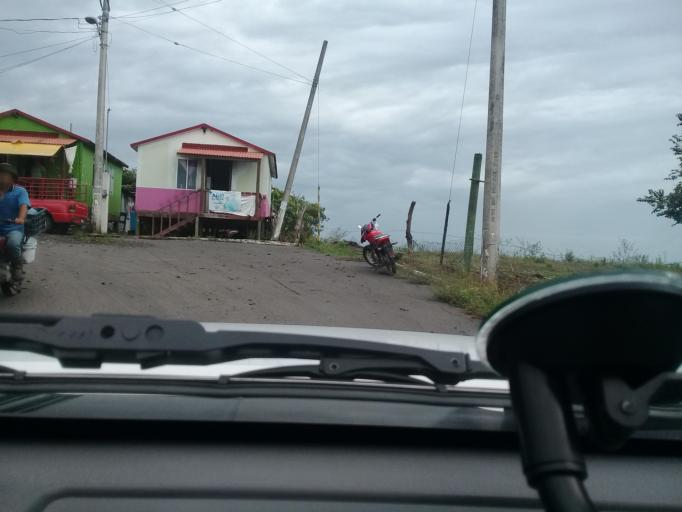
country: MX
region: Veracruz
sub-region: Puente Nacional
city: Cabezas
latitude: 19.3340
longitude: -96.3862
